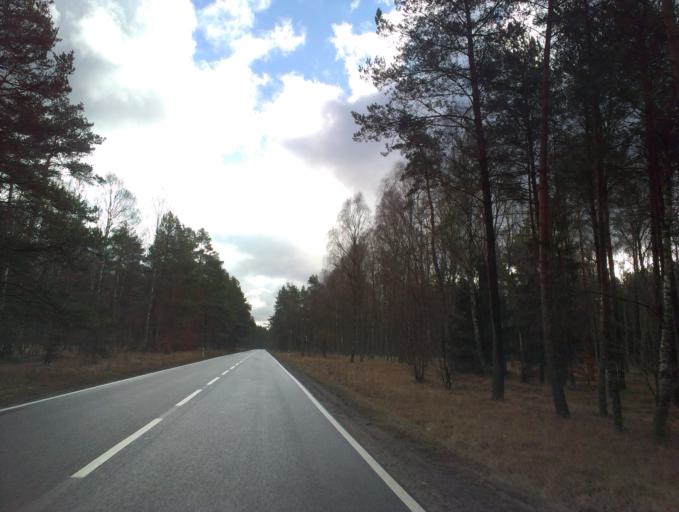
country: PL
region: Pomeranian Voivodeship
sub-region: Powiat czluchowski
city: Czarne
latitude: 53.7191
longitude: 16.8427
